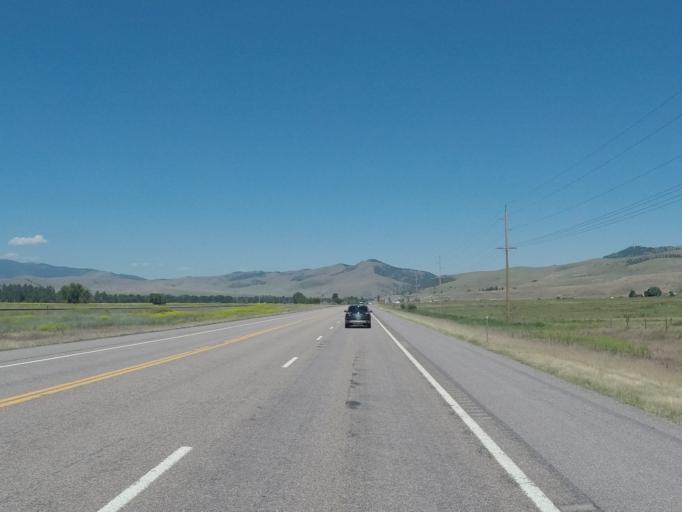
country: US
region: Montana
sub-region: Missoula County
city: Frenchtown
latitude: 47.2108
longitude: -114.1230
